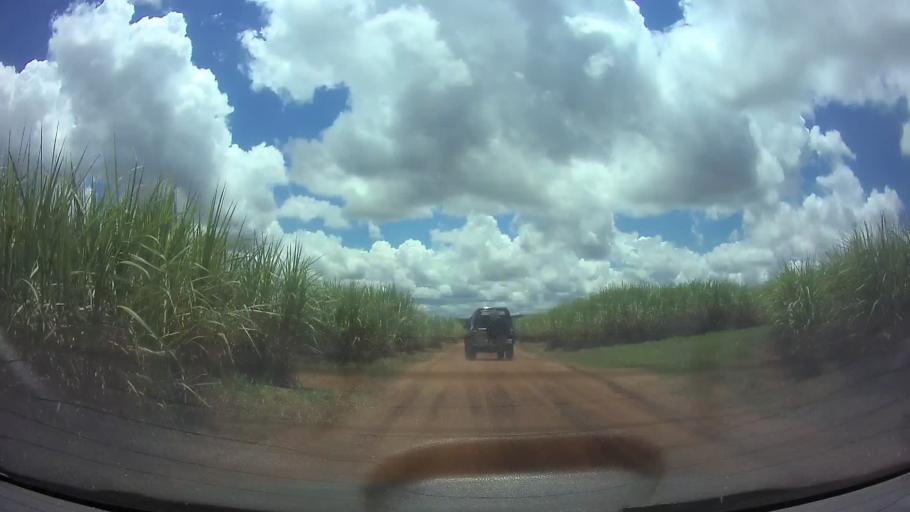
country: PY
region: Paraguari
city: La Colmena
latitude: -25.9631
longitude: -56.7629
